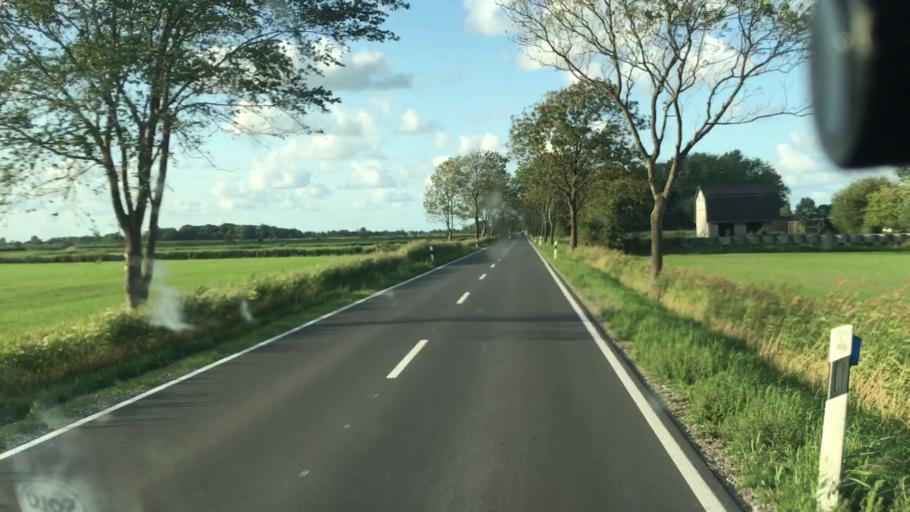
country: DE
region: Lower Saxony
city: Jever
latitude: 53.6299
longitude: 7.8616
